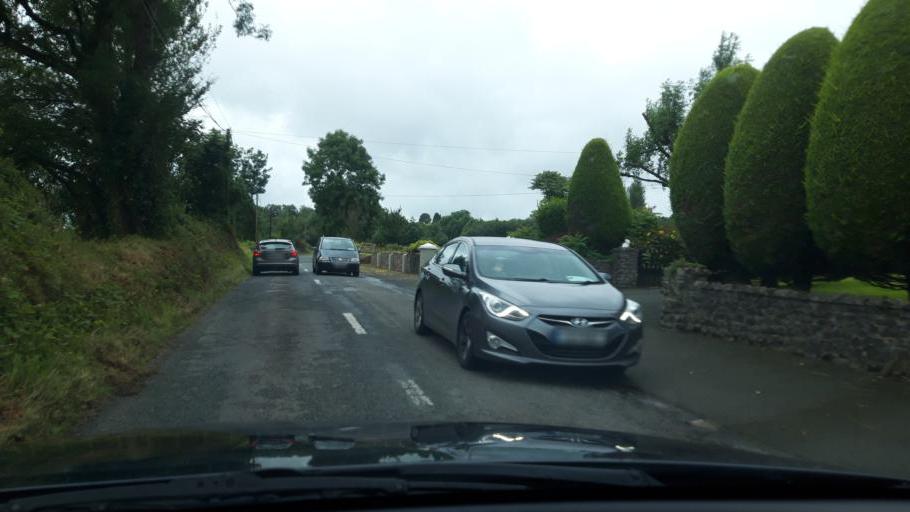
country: IE
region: Munster
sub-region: County Cork
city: Youghal
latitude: 52.1689
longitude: -7.8524
